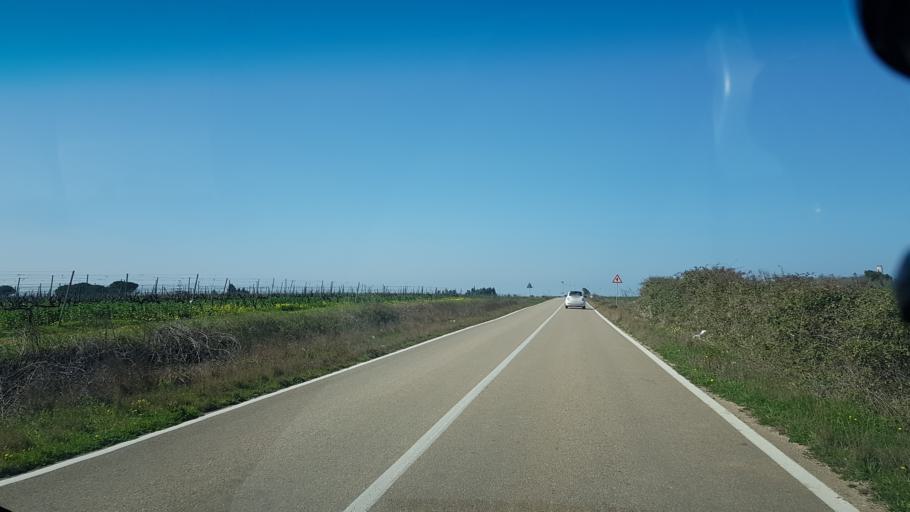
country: IT
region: Apulia
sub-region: Provincia di Brindisi
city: Torchiarolo
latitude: 40.5331
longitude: 18.0628
